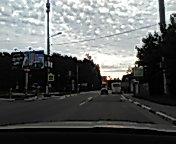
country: RU
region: Moskovskaya
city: Skhodnya
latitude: 55.9419
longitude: 37.2909
